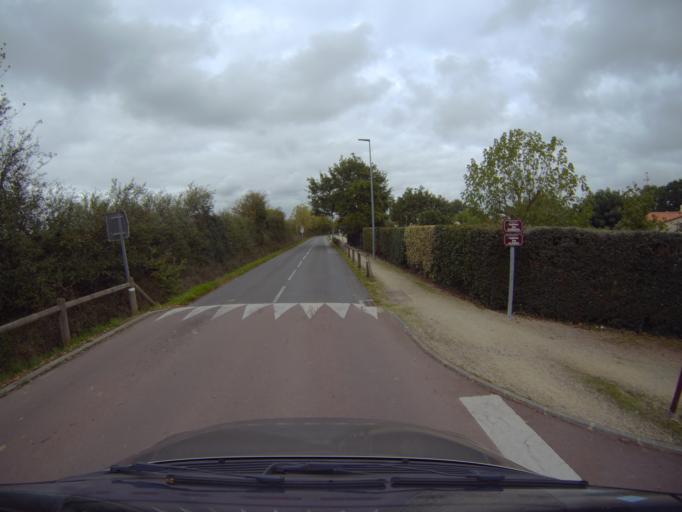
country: FR
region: Pays de la Loire
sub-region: Departement de la Loire-Atlantique
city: Clisson
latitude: 47.1001
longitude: -1.2691
